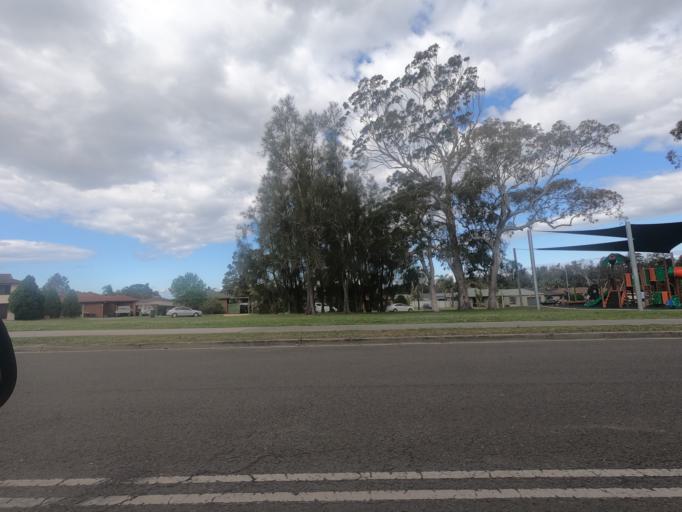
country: AU
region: New South Wales
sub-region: Wollongong
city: Dapto
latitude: -34.4877
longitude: 150.7795
